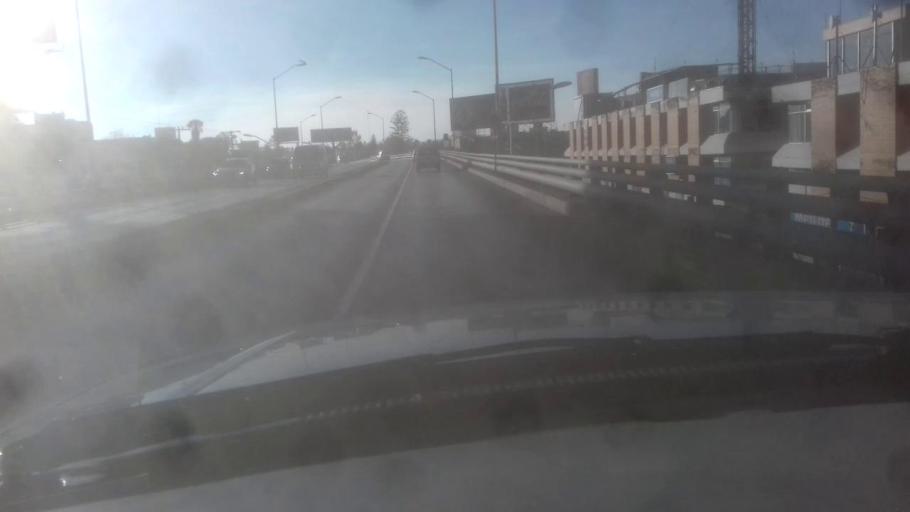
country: MX
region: Aguascalientes
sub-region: Aguascalientes
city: Aguascalientes
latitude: 21.8656
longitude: -102.2955
